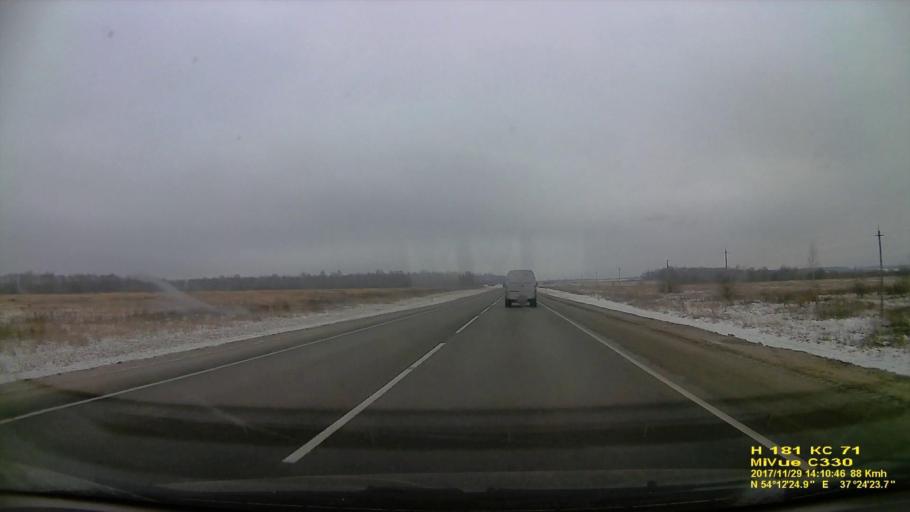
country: RU
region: Tula
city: Leninskiy
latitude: 54.2066
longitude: 37.4070
